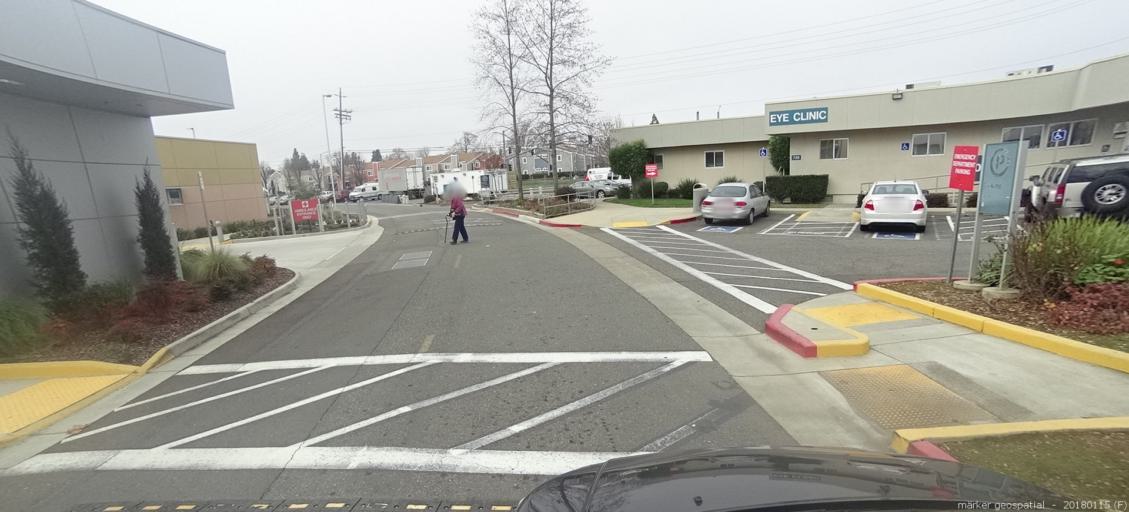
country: US
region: California
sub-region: Sacramento County
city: Rancho Cordova
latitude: 38.5734
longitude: -121.2947
